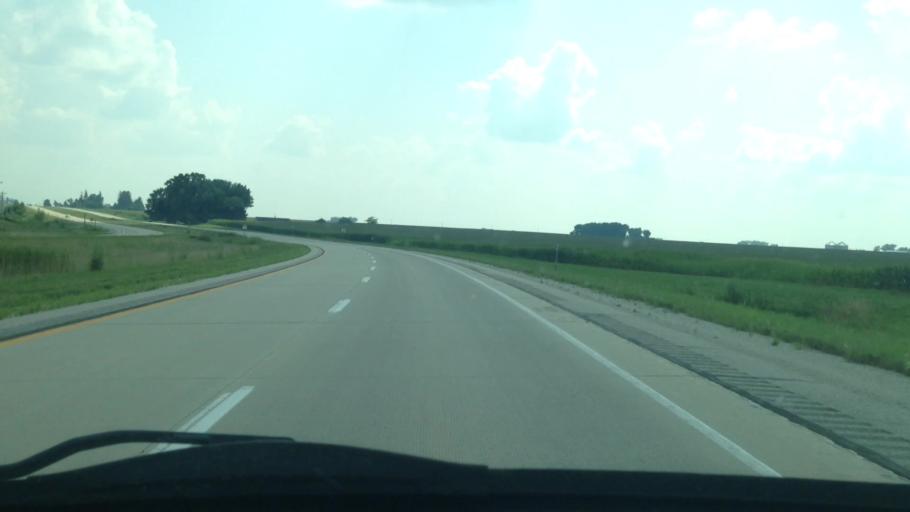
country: US
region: Iowa
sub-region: Bremer County
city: Tripoli
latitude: 42.8867
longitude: -92.3365
